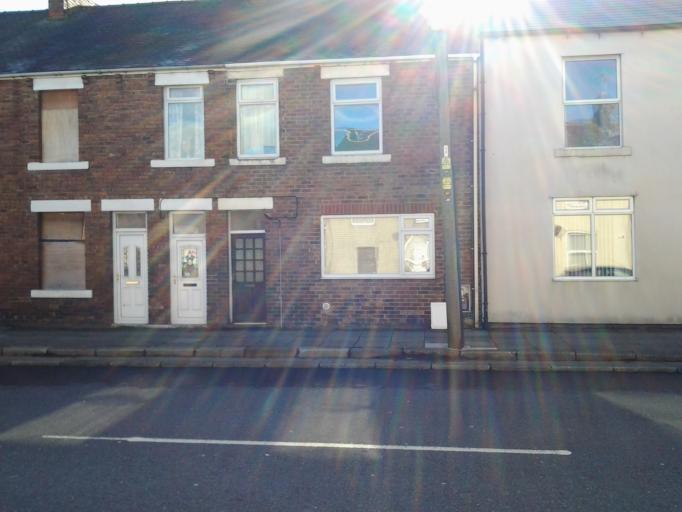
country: GB
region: England
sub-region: County Durham
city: Ushaw Moor
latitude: 54.7566
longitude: -1.6121
